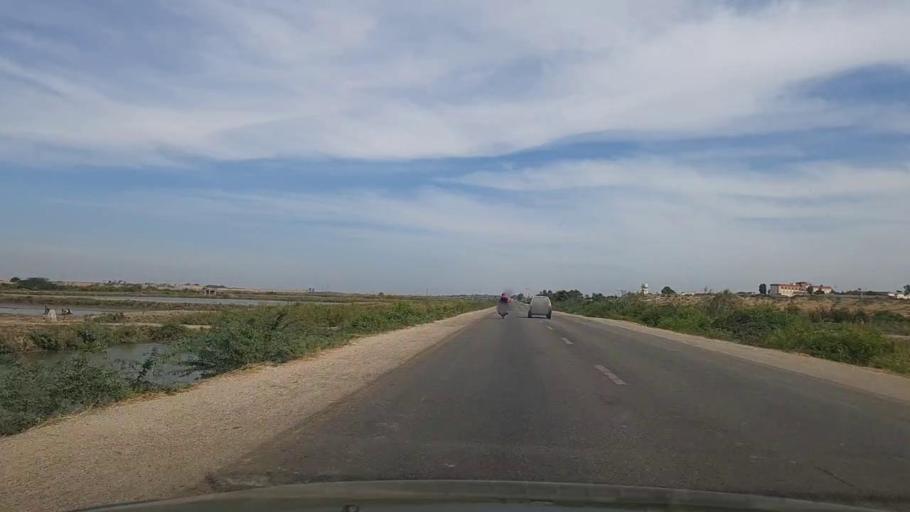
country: PK
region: Sindh
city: Thatta
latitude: 24.8155
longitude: 67.9804
